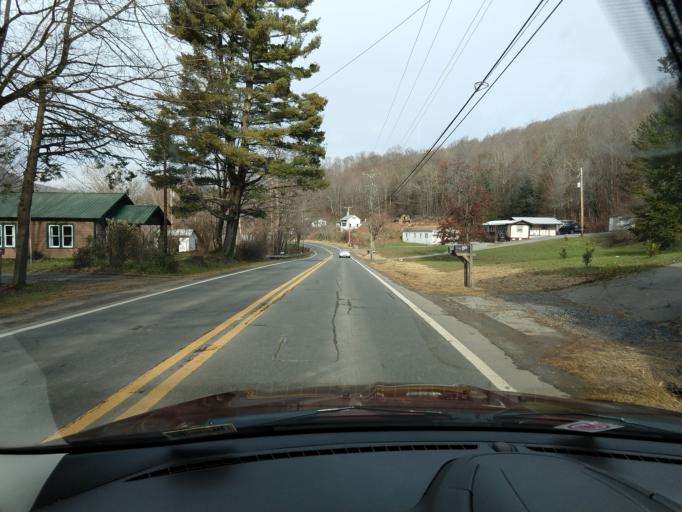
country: US
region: West Virginia
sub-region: Greenbrier County
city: Rainelle
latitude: 37.9672
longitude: -80.7000
